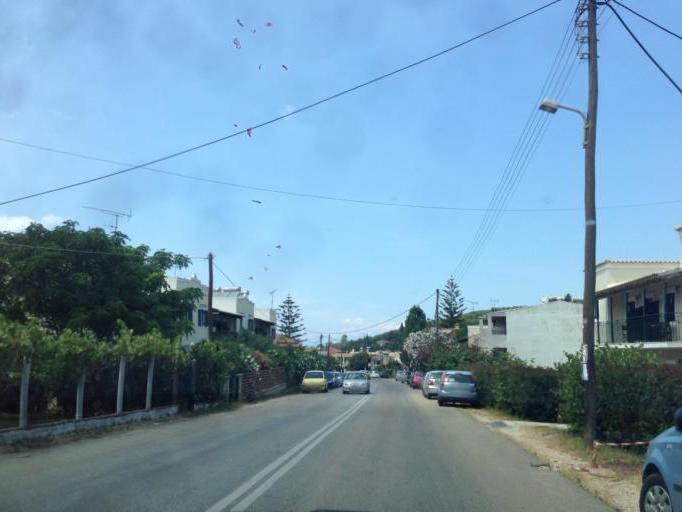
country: GR
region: Ionian Islands
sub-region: Nomos Kerkyras
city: Acharavi
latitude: 39.7864
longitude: 19.9203
